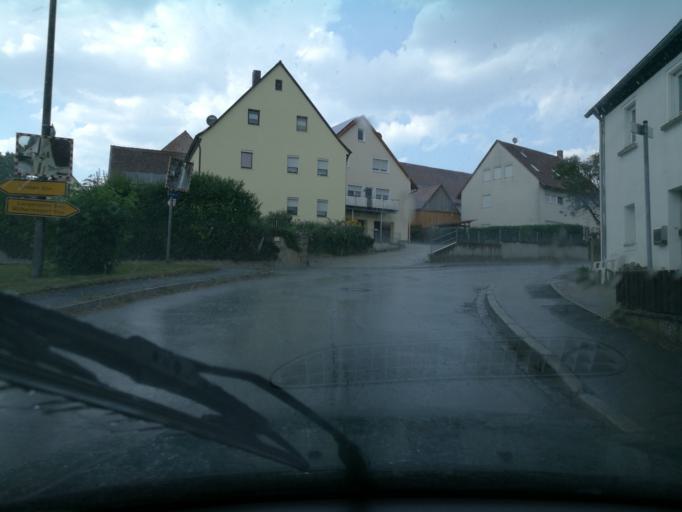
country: DE
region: Bavaria
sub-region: Regierungsbezirk Mittelfranken
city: Wilhermsdorf
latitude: 49.4436
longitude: 10.7343
